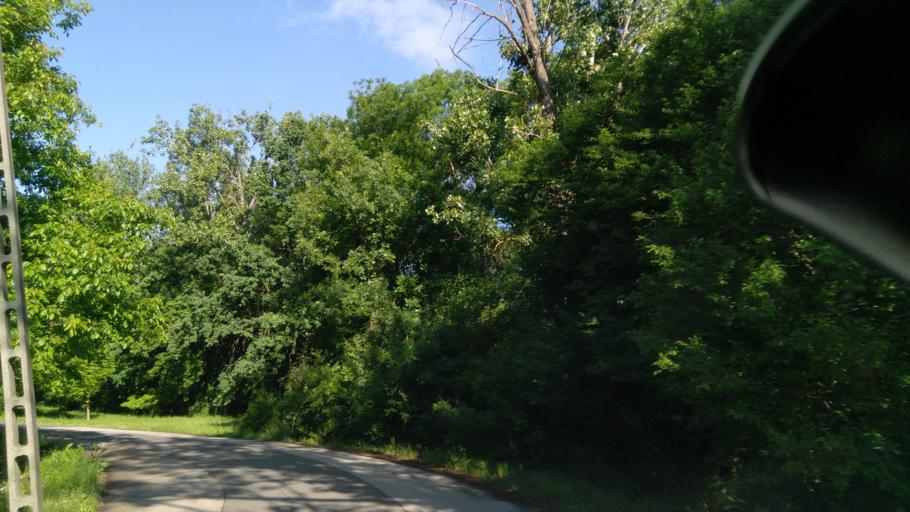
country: HU
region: Bekes
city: Bekes
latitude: 46.7820
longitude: 21.1338
